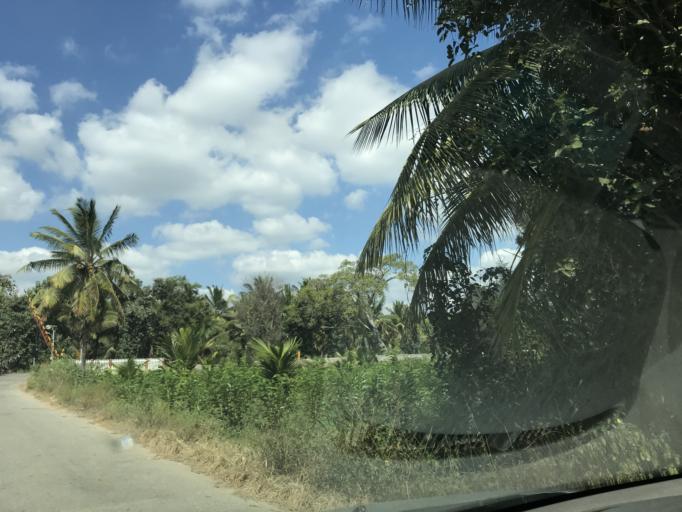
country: IN
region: Karnataka
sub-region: Mandya
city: Krishnarajpet
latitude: 12.7286
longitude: 76.3814
